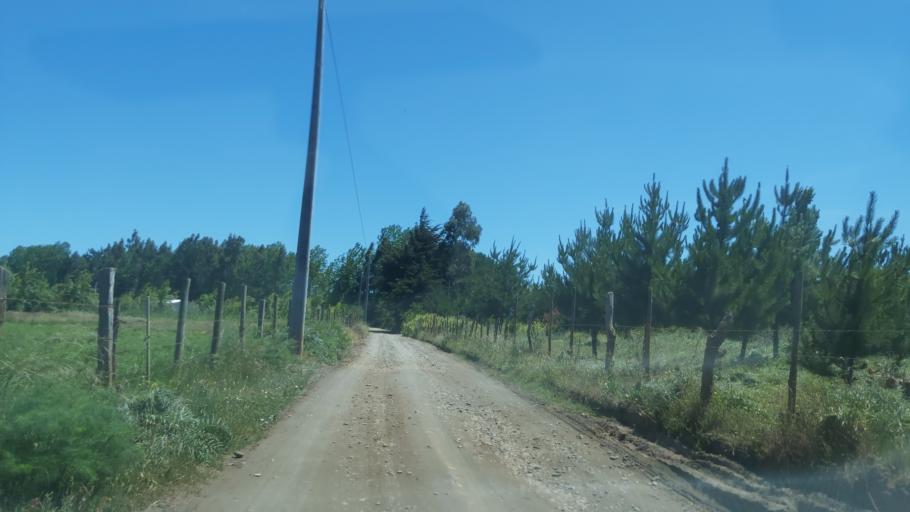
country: CL
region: Maule
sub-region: Provincia de Talca
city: Constitucion
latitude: -35.1630
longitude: -72.2655
